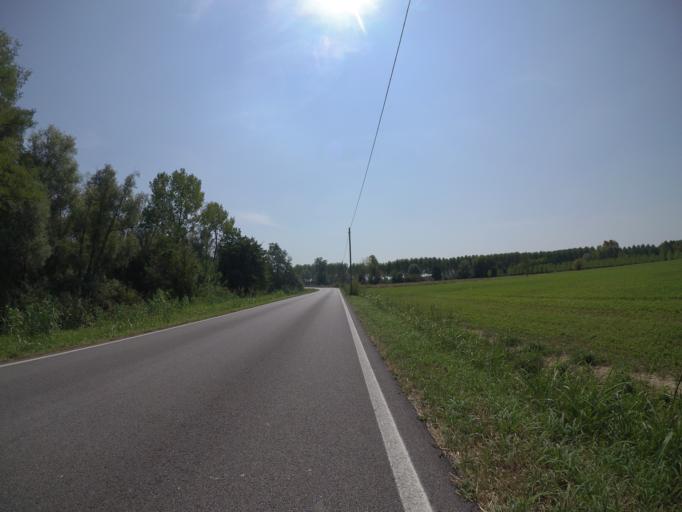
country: IT
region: Friuli Venezia Giulia
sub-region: Provincia di Udine
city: Pocenia
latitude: 45.8477
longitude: 13.0934
